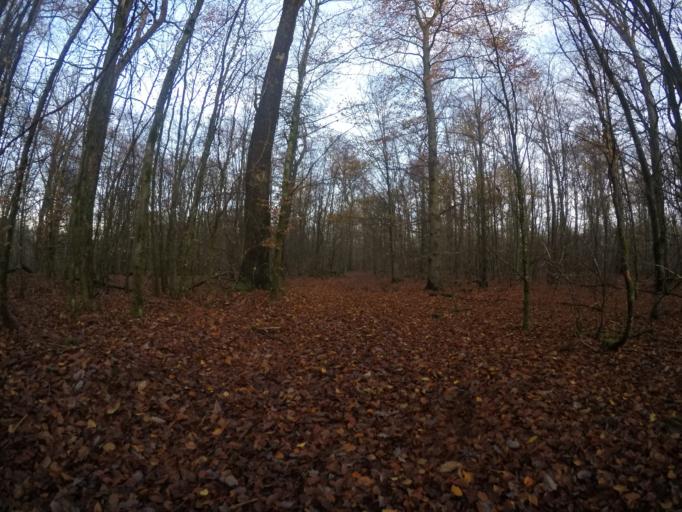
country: BE
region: Wallonia
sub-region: Province du Luxembourg
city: Habay-la-Vieille
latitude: 49.7458
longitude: 5.6730
